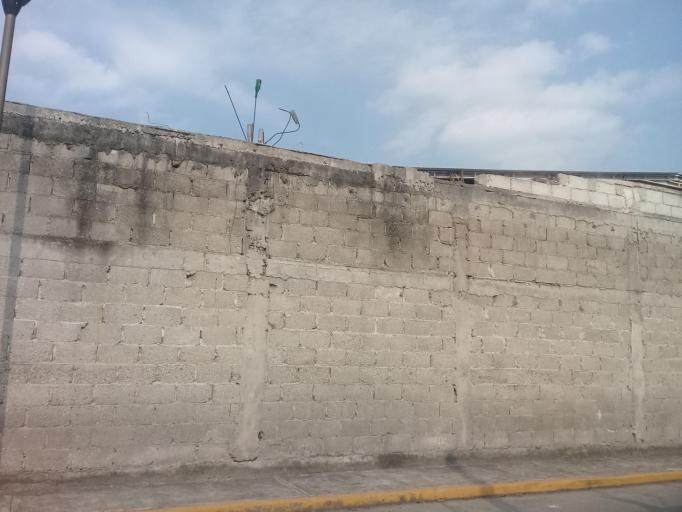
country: MX
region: Veracruz
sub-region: Ixhuatlancillo
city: Union y Progreso
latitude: 18.8705
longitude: -97.1072
